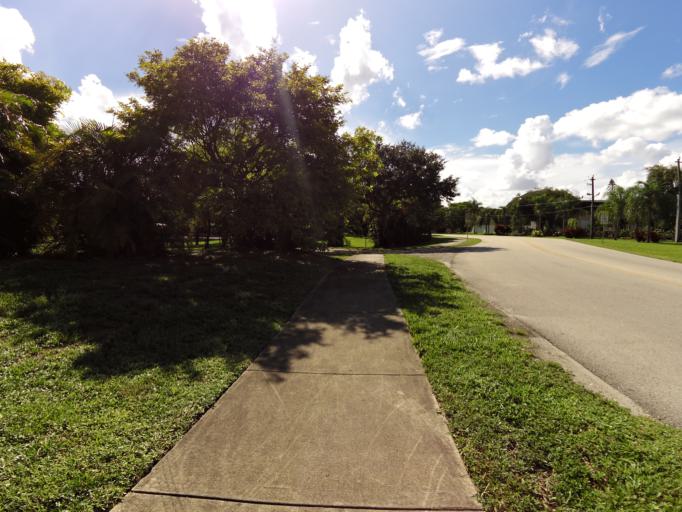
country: US
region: Florida
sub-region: Broward County
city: Davie
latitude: 26.0726
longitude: -80.2486
